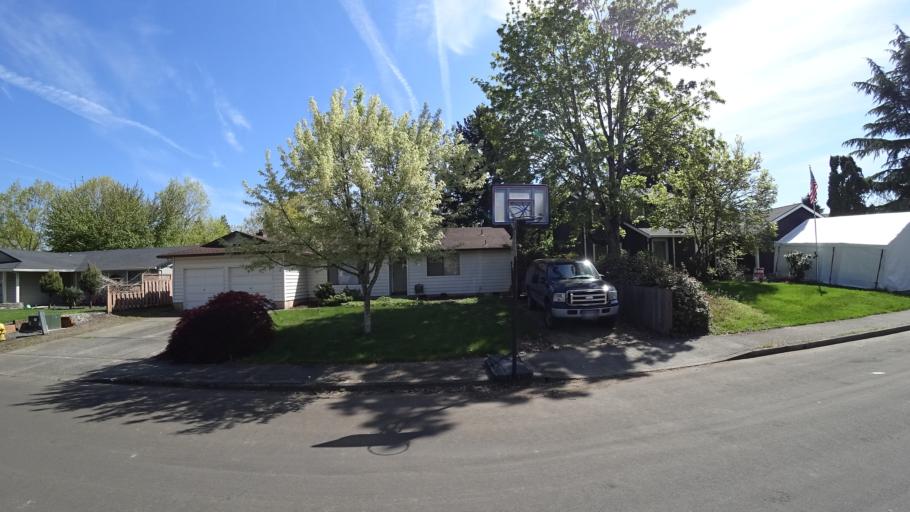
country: US
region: Oregon
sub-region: Washington County
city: Hillsboro
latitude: 45.5094
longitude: -122.9595
